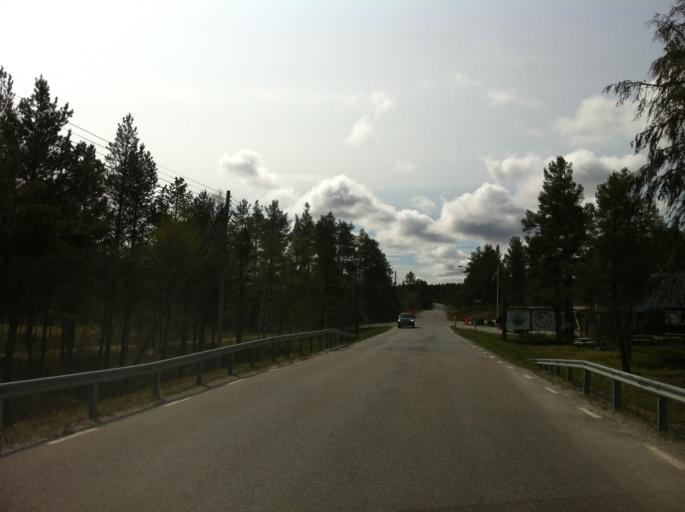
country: NO
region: Hedmark
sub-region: Engerdal
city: Engerdal
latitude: 62.4423
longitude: 12.6817
